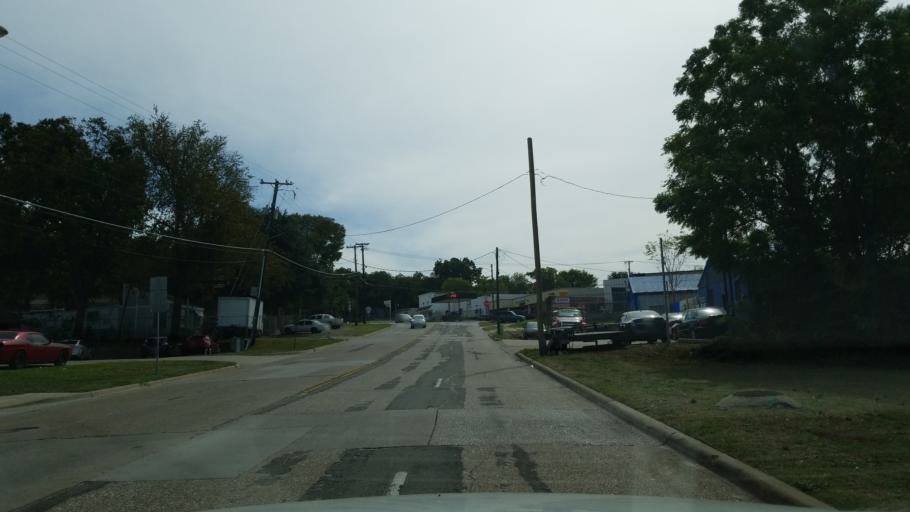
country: US
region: Texas
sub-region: Dallas County
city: Dallas
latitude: 32.7849
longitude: -96.7228
